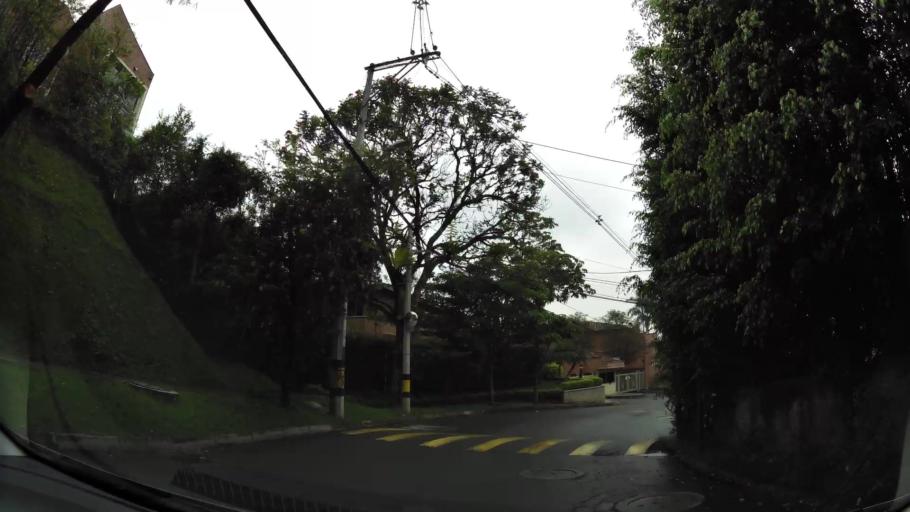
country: CO
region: Antioquia
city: Envigado
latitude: 6.1746
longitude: -75.5611
